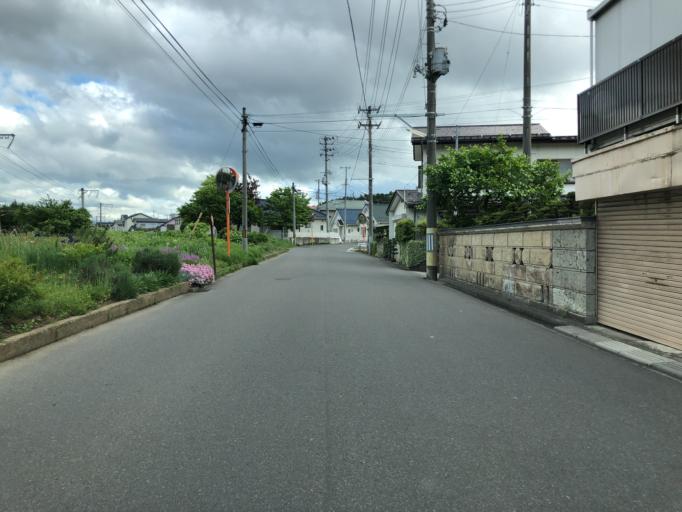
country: JP
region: Fukushima
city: Fukushima-shi
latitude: 37.7718
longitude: 140.4532
